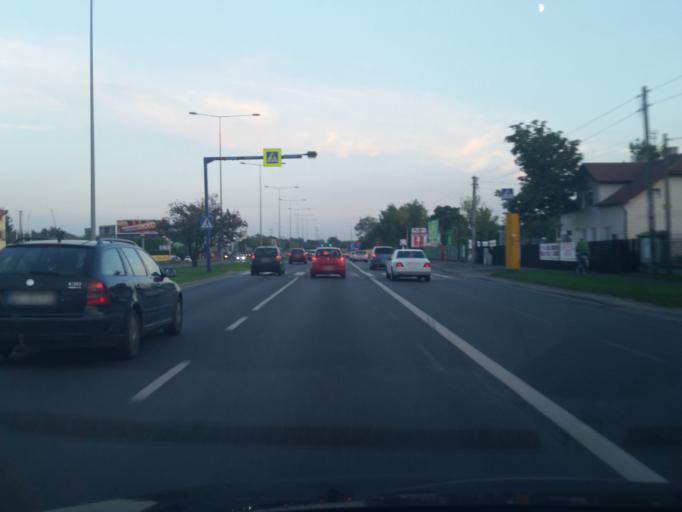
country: PL
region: Masovian Voivodeship
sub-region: Warszawa
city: Bialoleka
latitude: 52.3384
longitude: 20.9574
